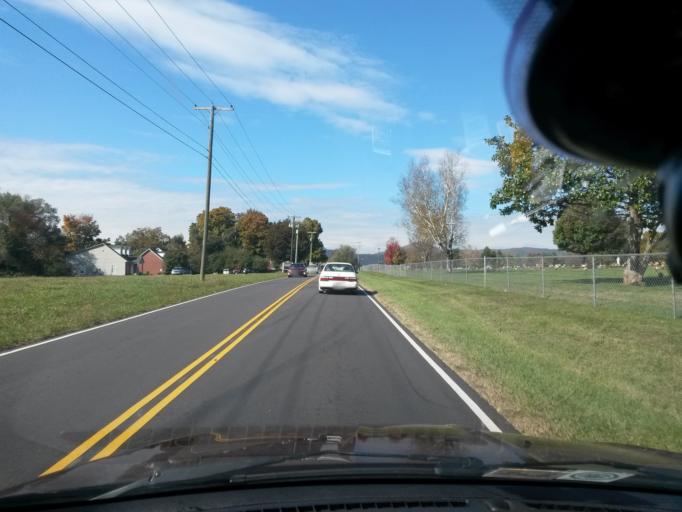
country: US
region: Virginia
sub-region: Roanoke County
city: Hollins
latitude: 37.3262
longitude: -79.9653
